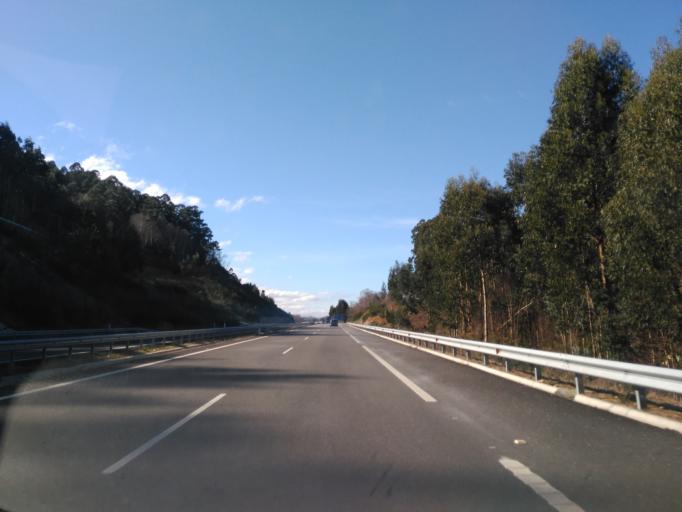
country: ES
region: Asturias
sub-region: Province of Asturias
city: Llanes
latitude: 43.3925
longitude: -4.6324
